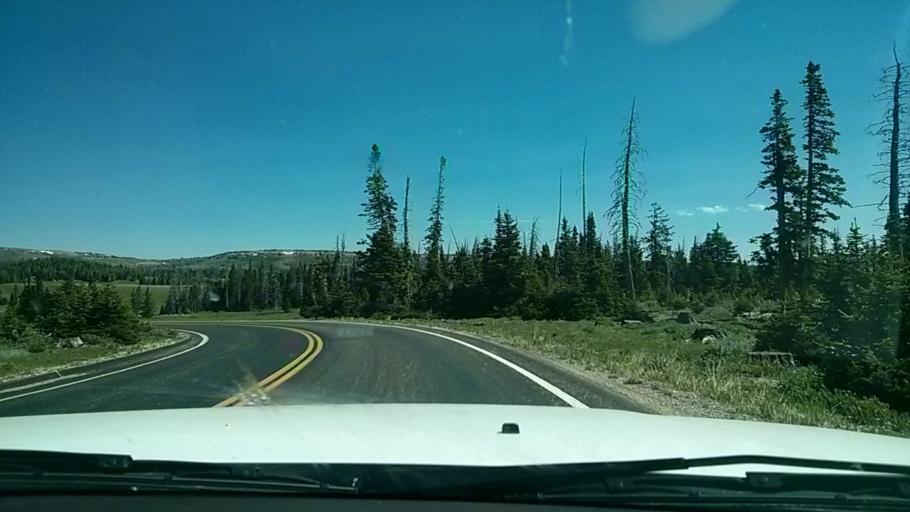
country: US
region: Utah
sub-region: Iron County
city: Parowan
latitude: 37.6425
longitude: -112.8215
